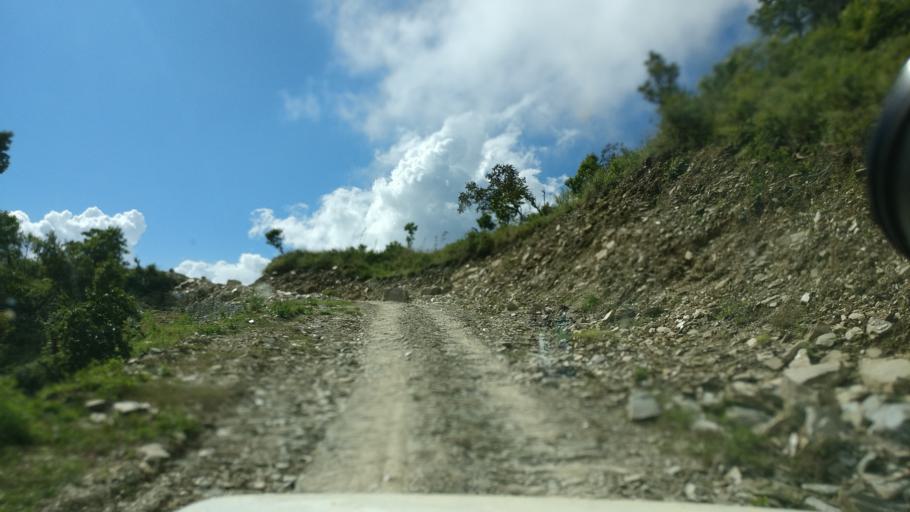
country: NP
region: Western Region
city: Baglung
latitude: 28.2772
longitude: 83.6409
